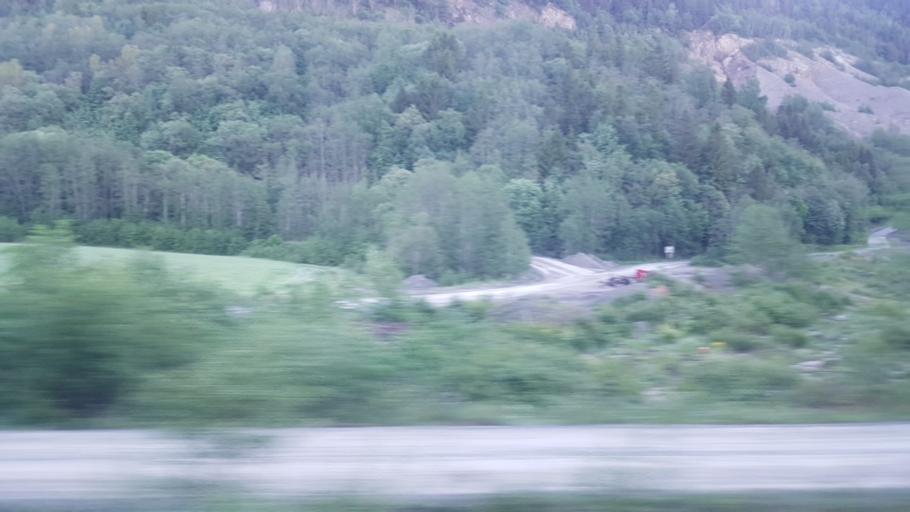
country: NO
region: Sor-Trondelag
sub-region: Melhus
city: Melhus
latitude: 63.2732
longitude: 10.2675
